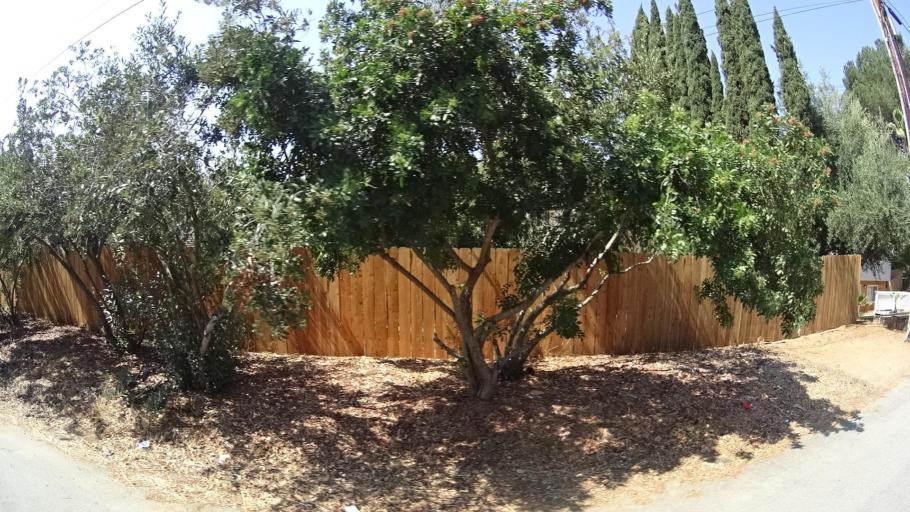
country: US
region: California
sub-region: San Diego County
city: Bonsall
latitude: 33.2490
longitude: -117.2355
